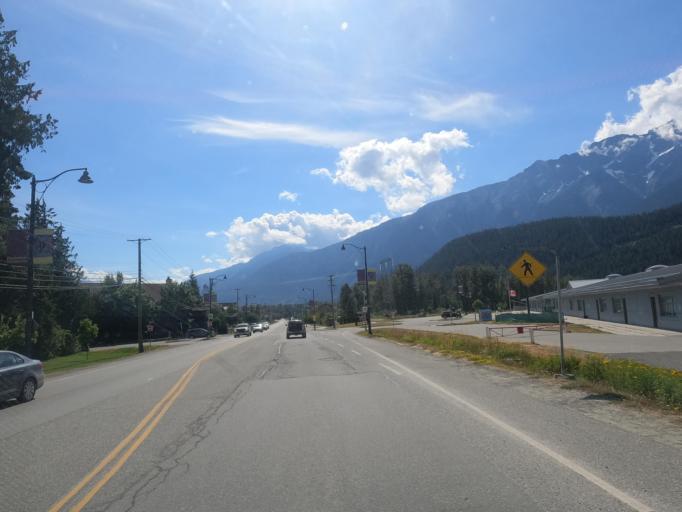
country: CA
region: British Columbia
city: Pemberton
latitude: 50.3198
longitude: -122.8048
